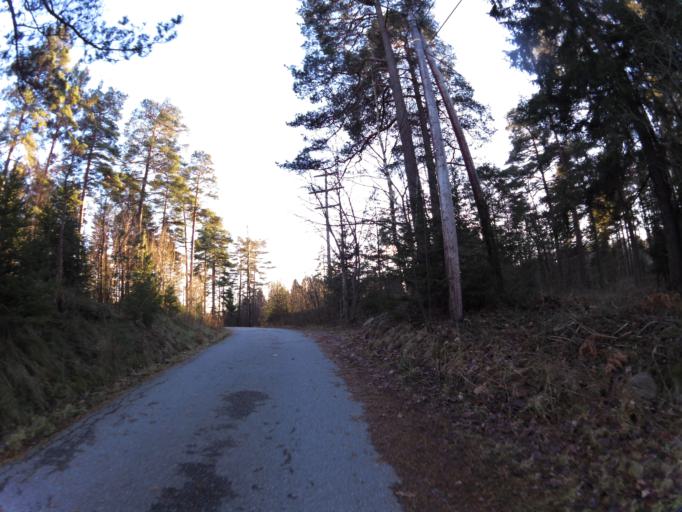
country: NO
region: Ostfold
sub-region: Fredrikstad
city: Fredrikstad
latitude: 59.2420
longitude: 10.9645
